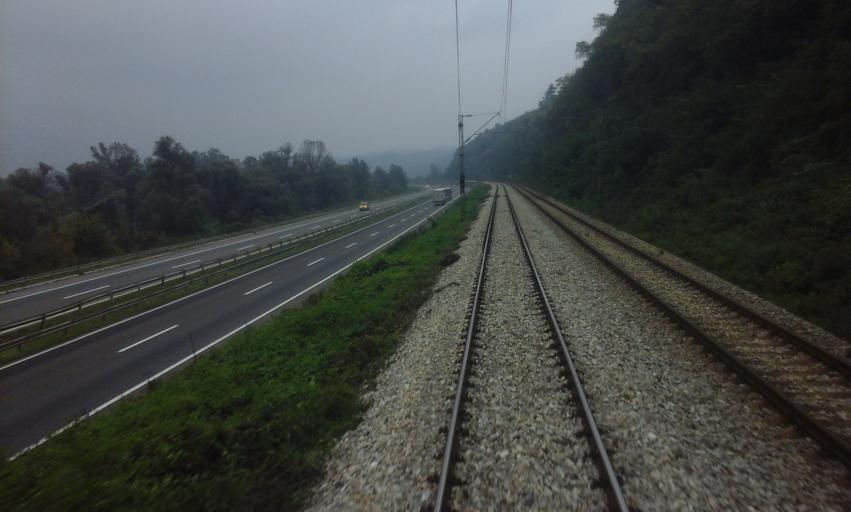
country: RS
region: Central Serbia
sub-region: Pomoravski Okrug
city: Jagodina
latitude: 44.0700
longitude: 21.1948
